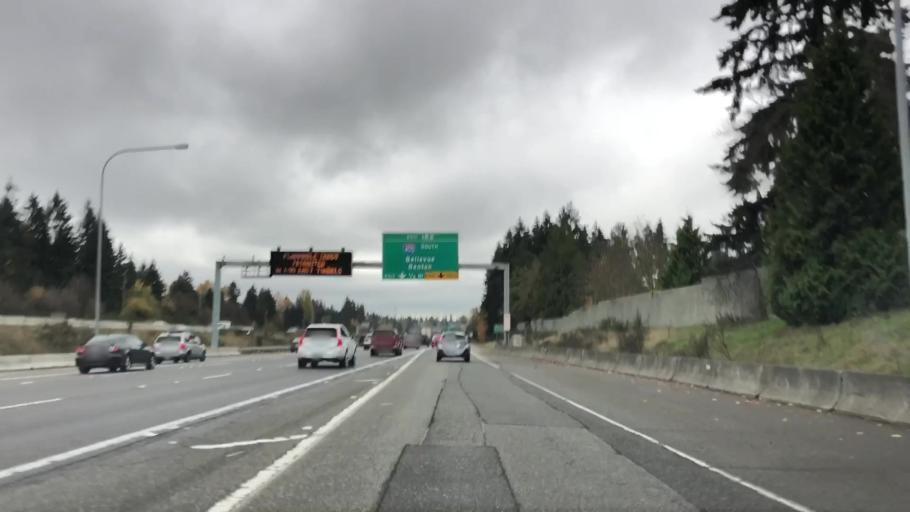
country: US
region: Washington
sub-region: Snohomish County
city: Martha Lake
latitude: 47.8449
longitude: -122.2592
